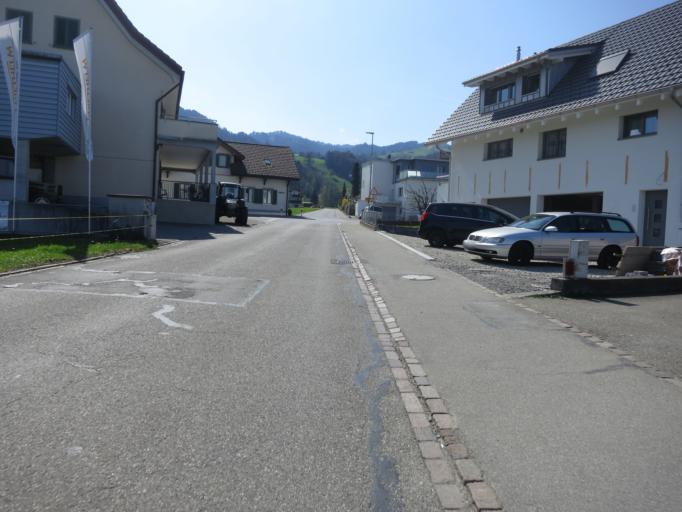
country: CH
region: Schwyz
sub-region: Bezirk March
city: Lachen
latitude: 47.1799
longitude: 8.8707
